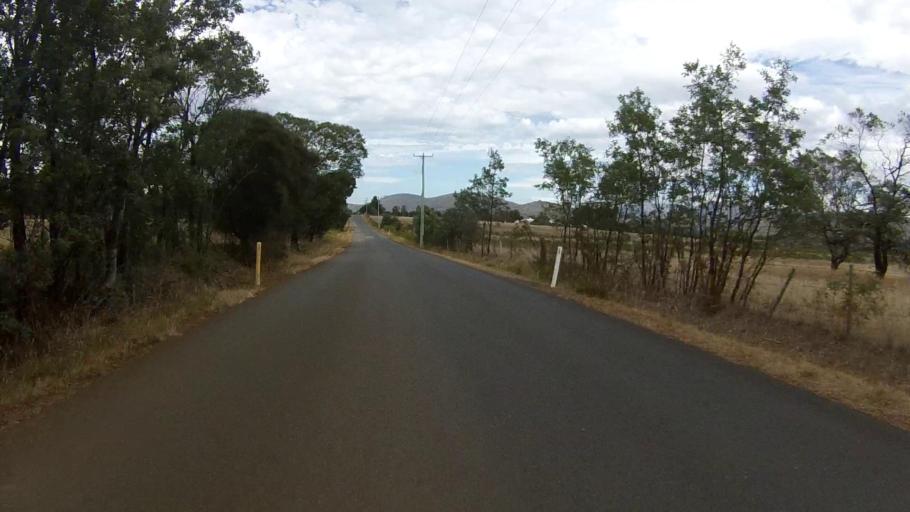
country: AU
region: Tasmania
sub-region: Clarence
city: Cambridge
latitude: -42.7148
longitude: 147.4527
